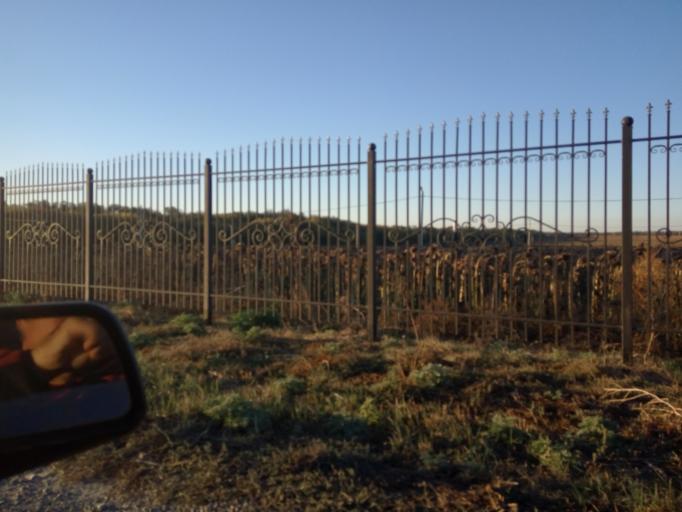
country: RU
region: Rostov
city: Temernik
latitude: 47.3576
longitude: 39.7448
